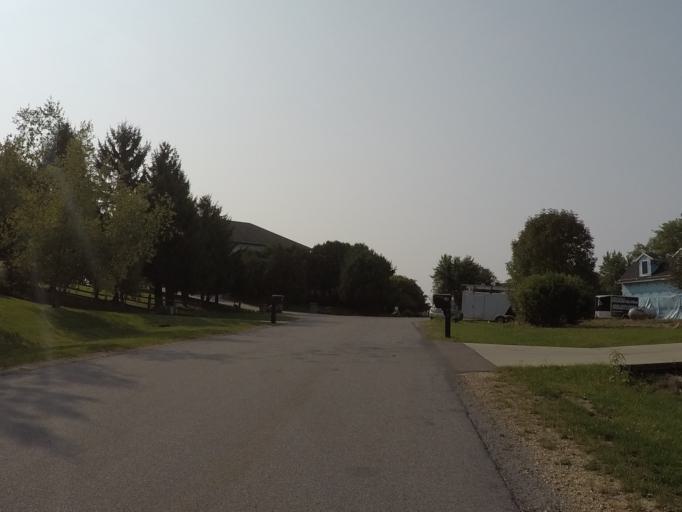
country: US
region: Wisconsin
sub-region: Dane County
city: Verona
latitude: 43.0448
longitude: -89.5297
